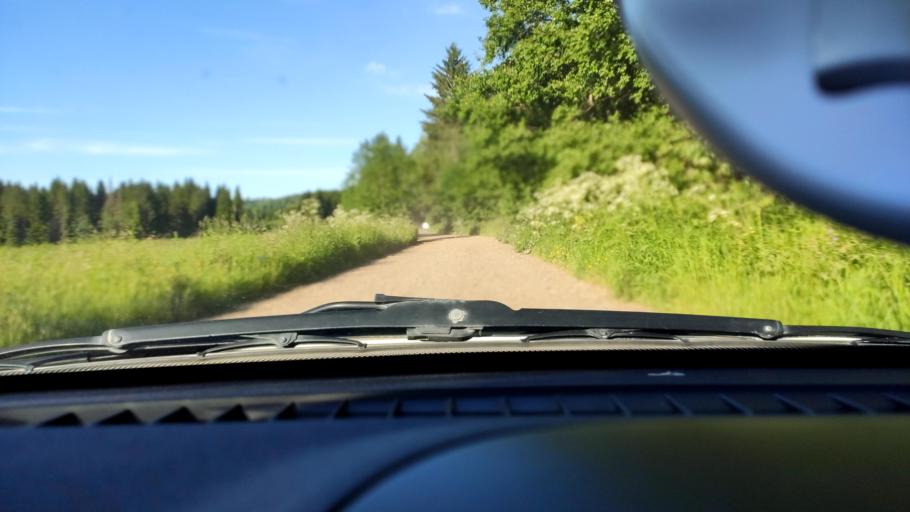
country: RU
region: Perm
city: Bershet'
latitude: 57.6962
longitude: 56.4059
